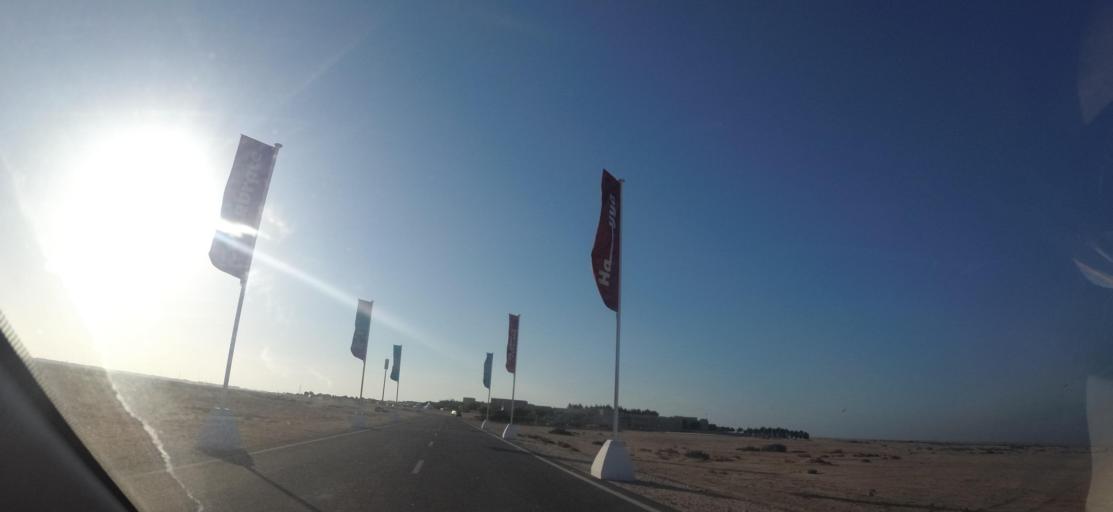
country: QA
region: Madinat ash Shamal
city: Ar Ru'ays
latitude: 26.1550
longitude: 51.2464
